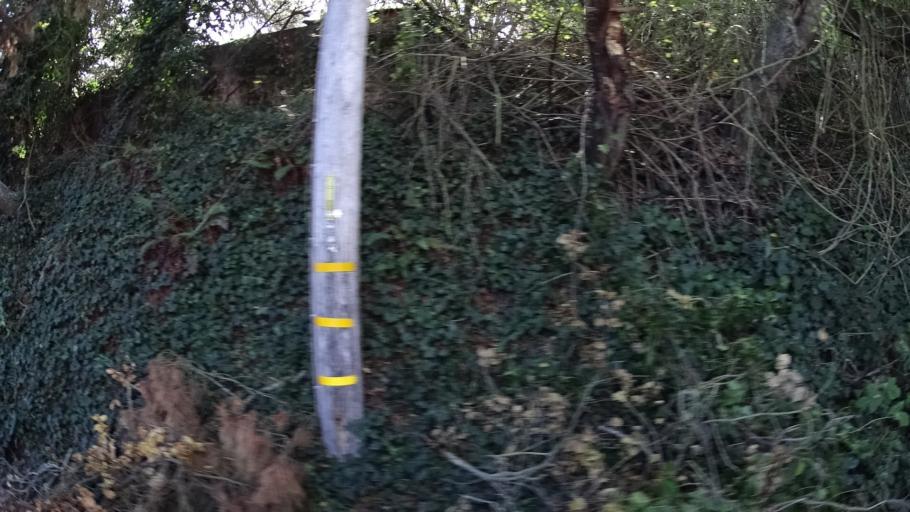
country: US
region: California
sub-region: Alameda County
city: Piedmont
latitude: 37.8422
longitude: -122.2127
